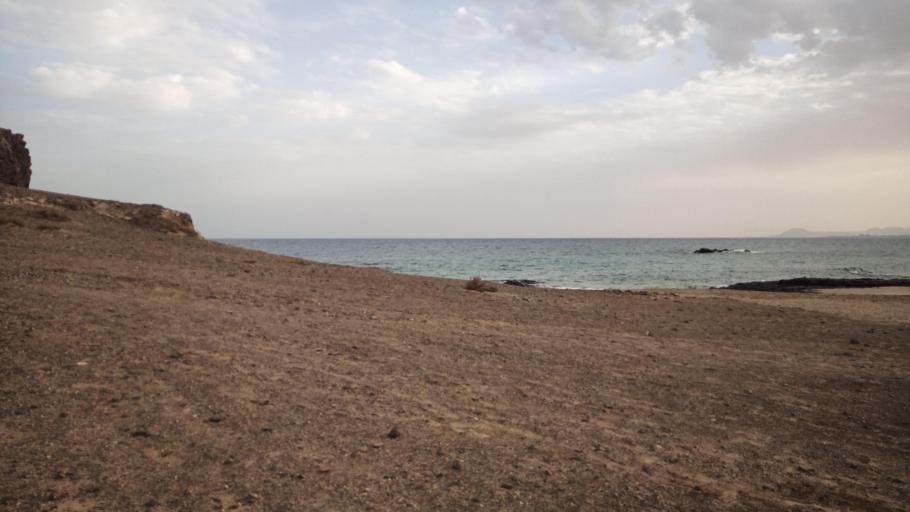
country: ES
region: Canary Islands
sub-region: Provincia de Las Palmas
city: Playa Blanca
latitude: 28.8445
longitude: -13.7811
